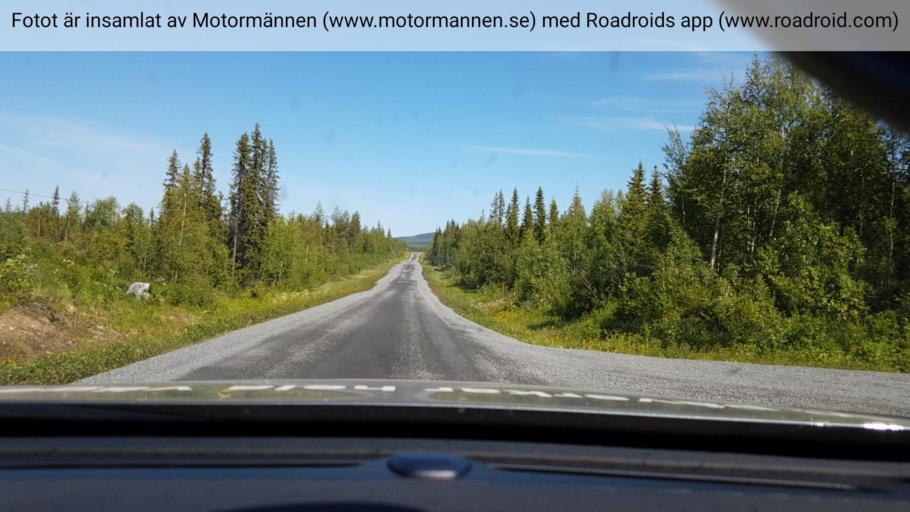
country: SE
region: Vaesterbotten
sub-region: Vilhelmina Kommun
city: Sjoberg
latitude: 64.7904
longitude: 15.9793
